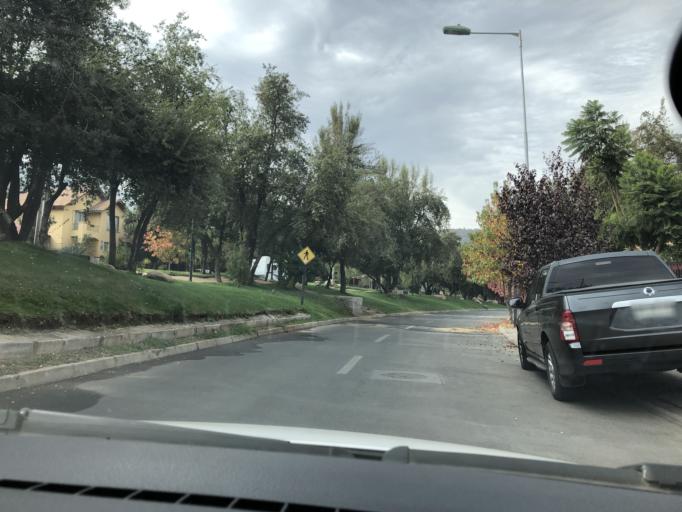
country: CL
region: Santiago Metropolitan
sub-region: Provincia de Cordillera
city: Puente Alto
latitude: -33.5836
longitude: -70.5120
